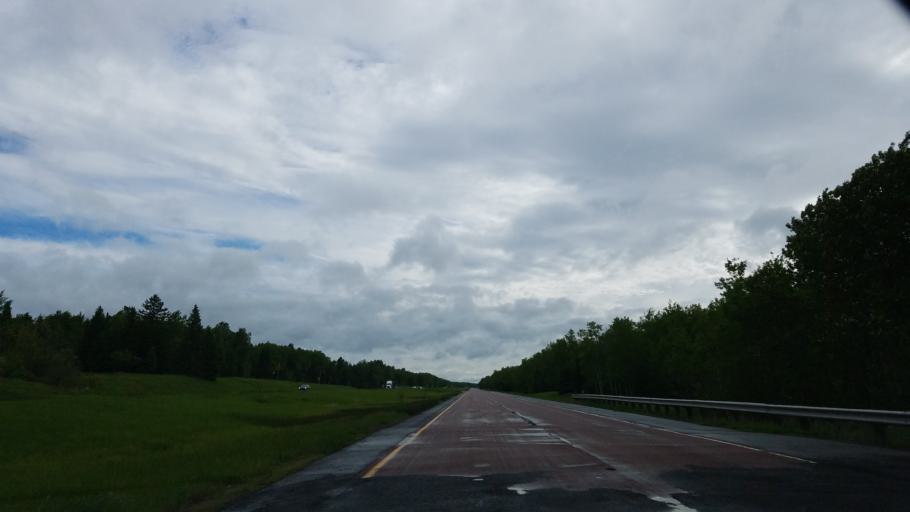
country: US
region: Minnesota
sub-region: Saint Louis County
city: Arnold
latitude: 46.8693
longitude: -91.9567
